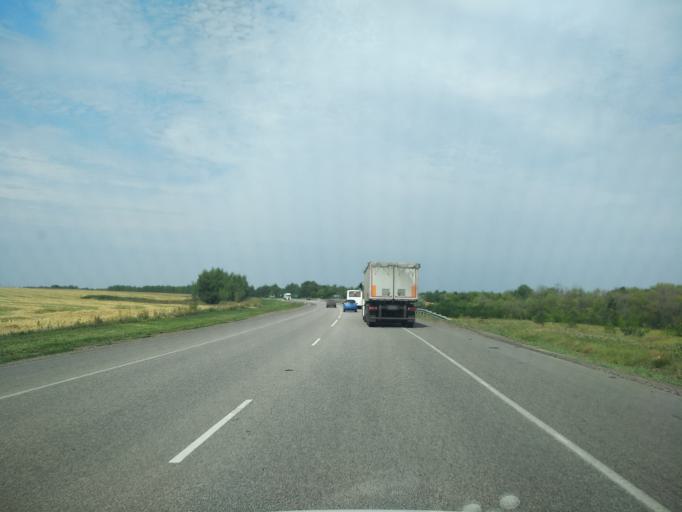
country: RU
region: Voronezj
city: Novaya Usman'
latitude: 51.7003
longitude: 39.4259
